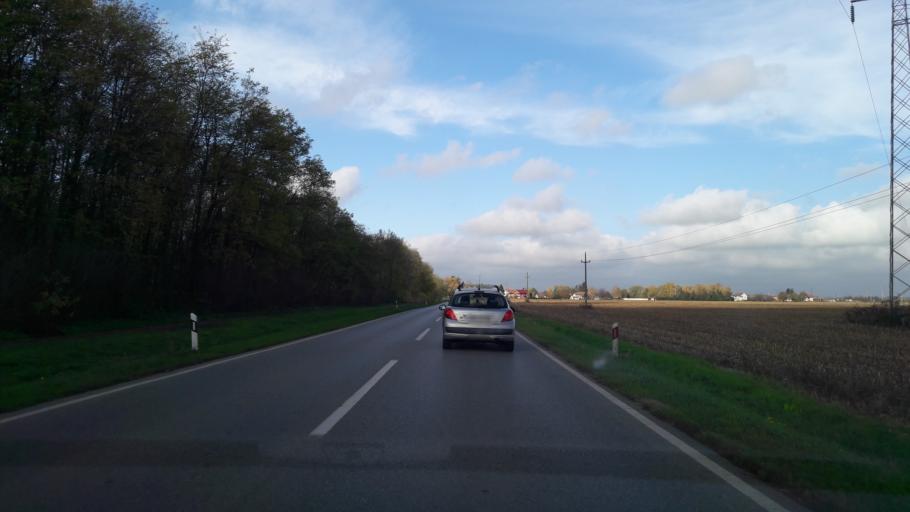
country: HR
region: Osjecko-Baranjska
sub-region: Grad Osijek
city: Bilje
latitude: 45.6165
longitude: 18.7289
